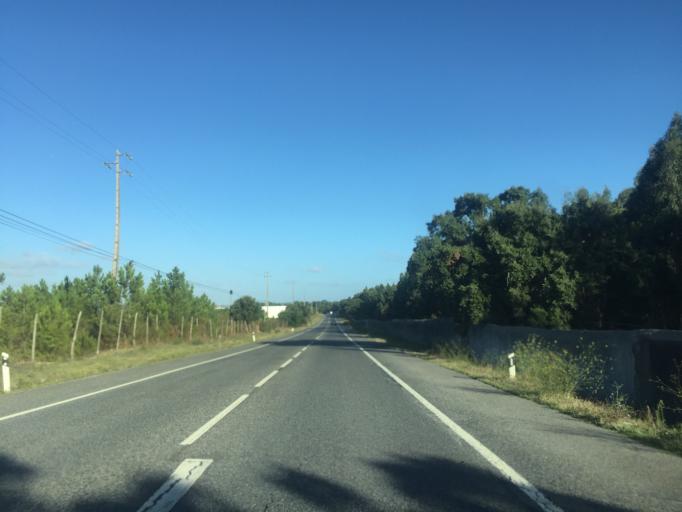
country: PT
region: Lisbon
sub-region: Azambuja
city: Alcoentre
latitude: 39.1769
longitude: -8.9373
